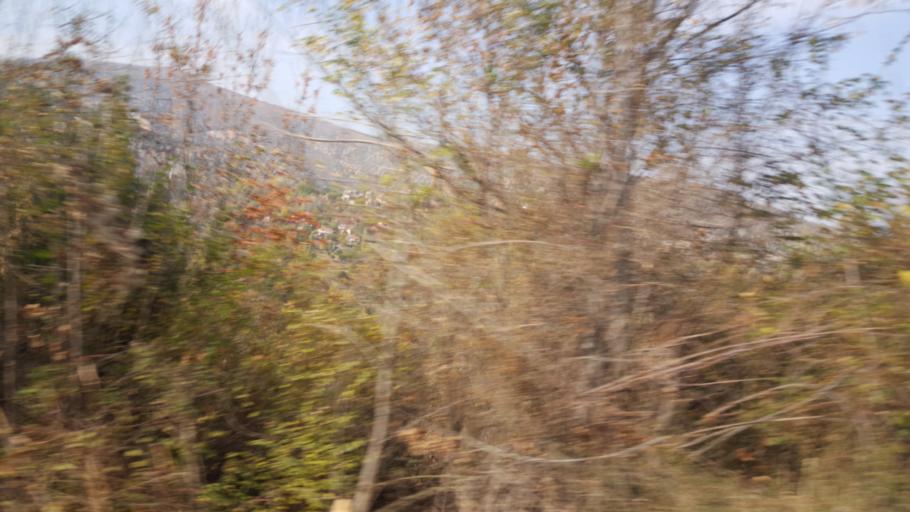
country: TR
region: Eskisehir
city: Mihaliccik
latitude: 39.9879
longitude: 31.3490
